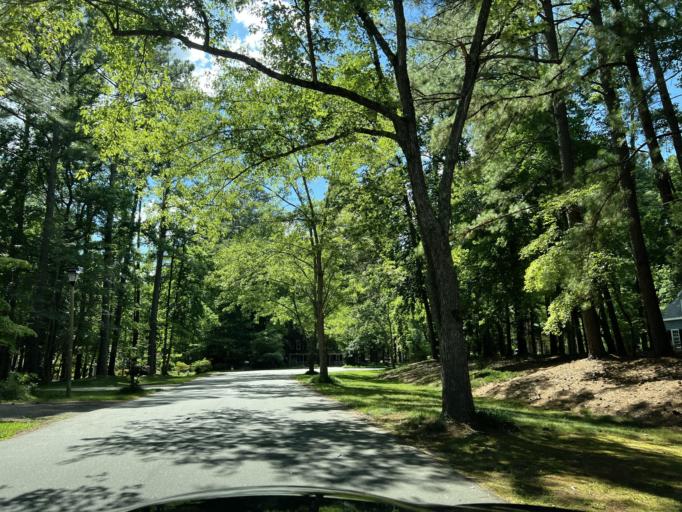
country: US
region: North Carolina
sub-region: Wake County
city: Wake Forest
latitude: 35.9443
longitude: -78.6348
